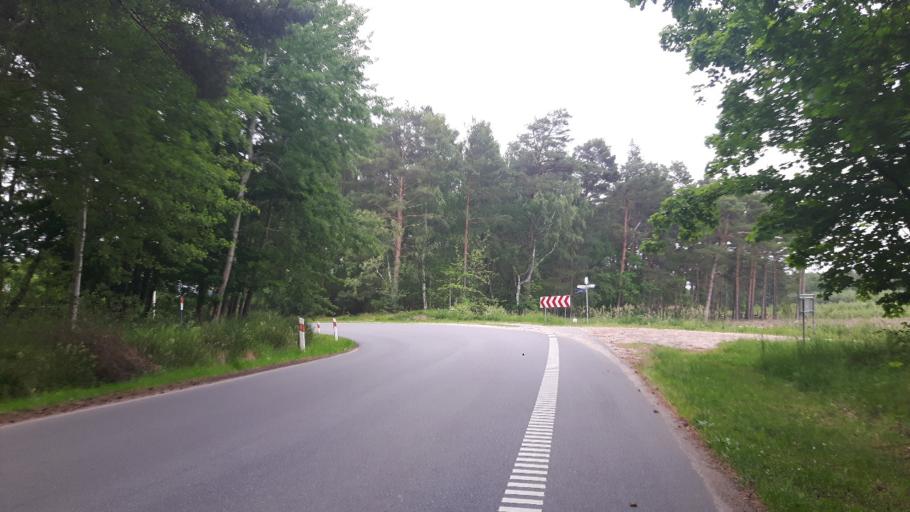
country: PL
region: Pomeranian Voivodeship
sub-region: Powiat slupski
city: Smoldzino
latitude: 54.6498
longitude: 17.0495
